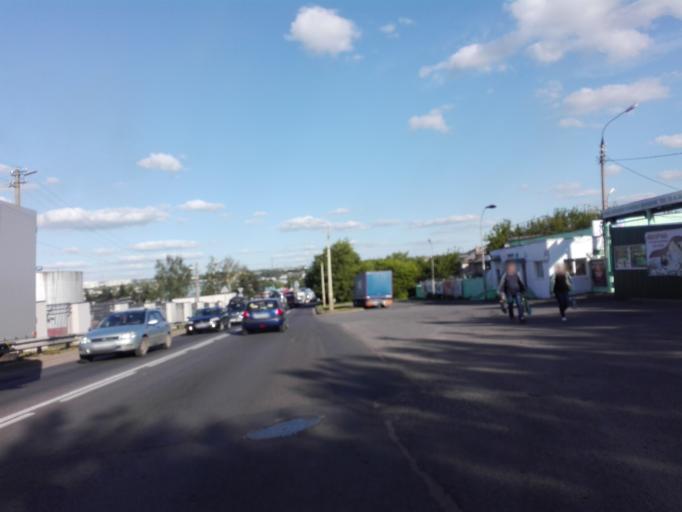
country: RU
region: Orjol
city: Orel
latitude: 52.9379
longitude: 36.0545
